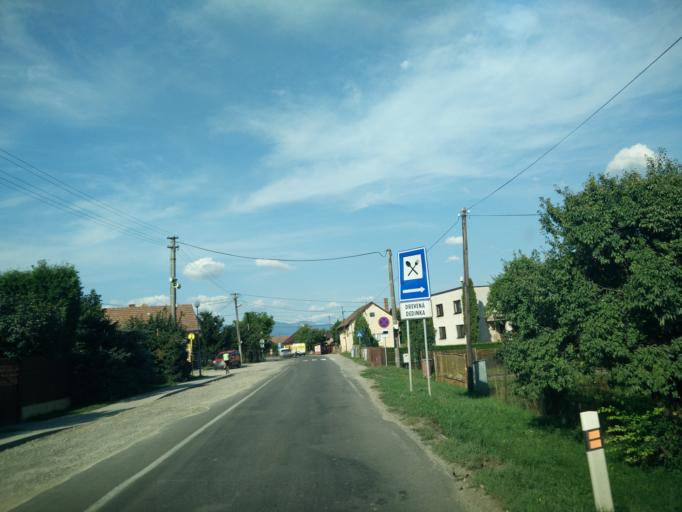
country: SK
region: Zilinsky
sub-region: Okres Martin
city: Martin
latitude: 48.9940
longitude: 18.8703
